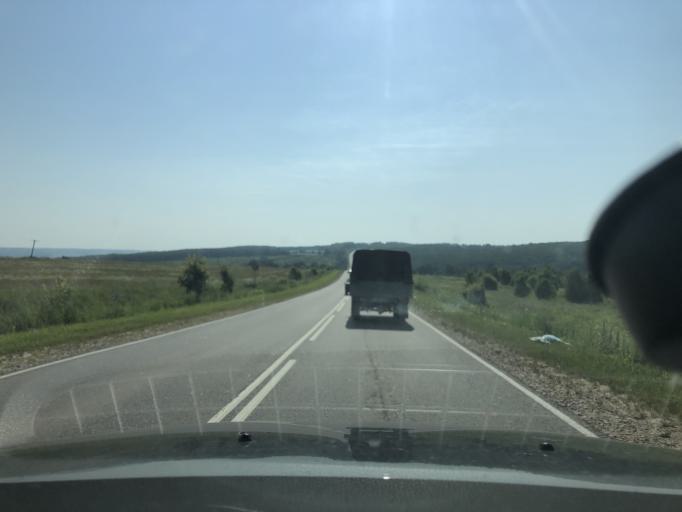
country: RU
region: Tula
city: Dubna
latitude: 54.1322
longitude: 37.0323
